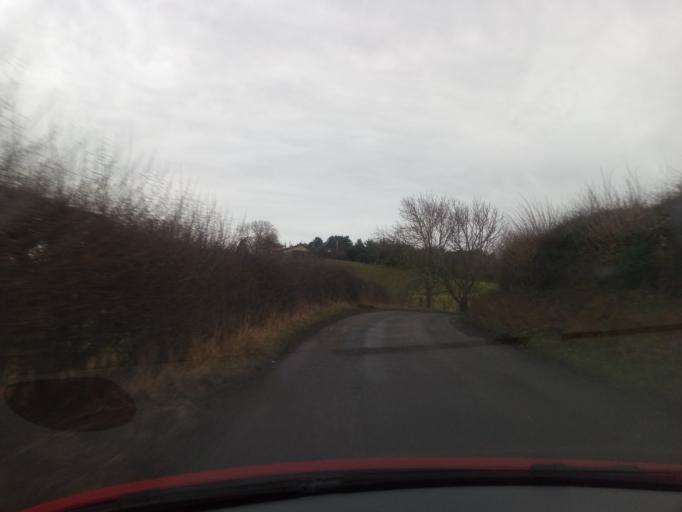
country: GB
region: England
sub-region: Northumberland
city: Wooler
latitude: 55.5492
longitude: -2.0264
